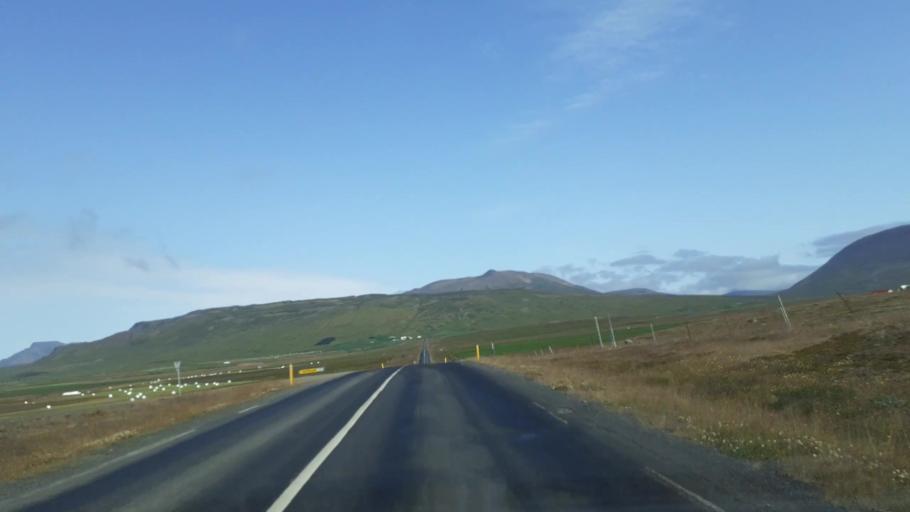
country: IS
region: Northwest
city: Saudarkrokur
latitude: 65.7093
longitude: -20.2301
